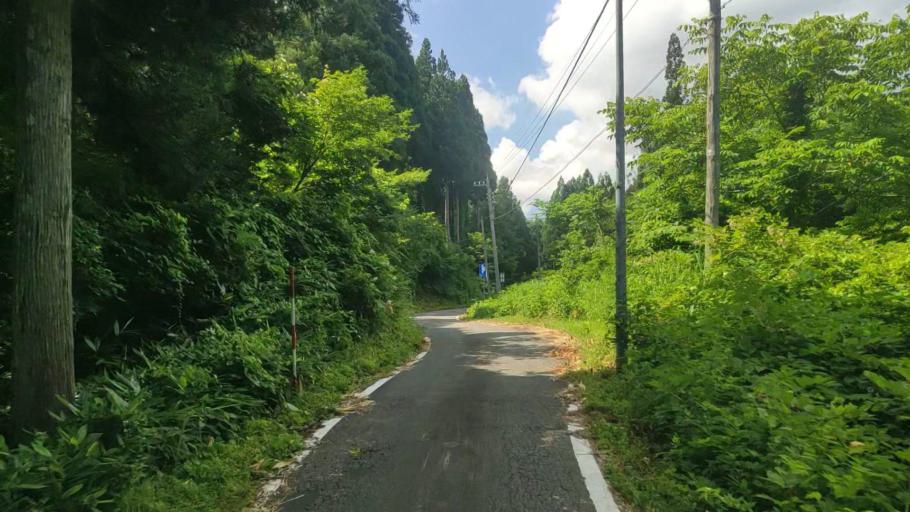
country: JP
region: Fukui
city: Katsuyama
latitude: 36.2123
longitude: 136.5284
